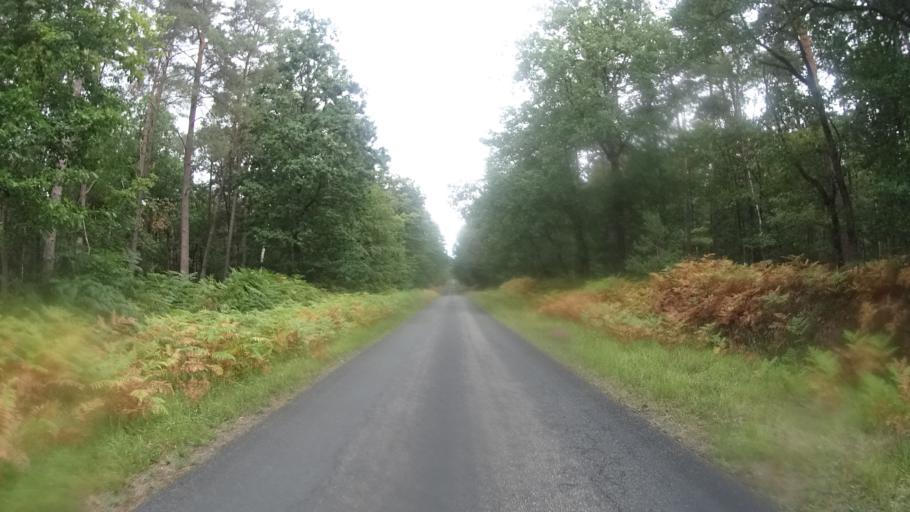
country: FR
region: Centre
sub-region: Departement du Loiret
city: Vitry-aux-Loges
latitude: 48.0270
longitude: 2.2588
